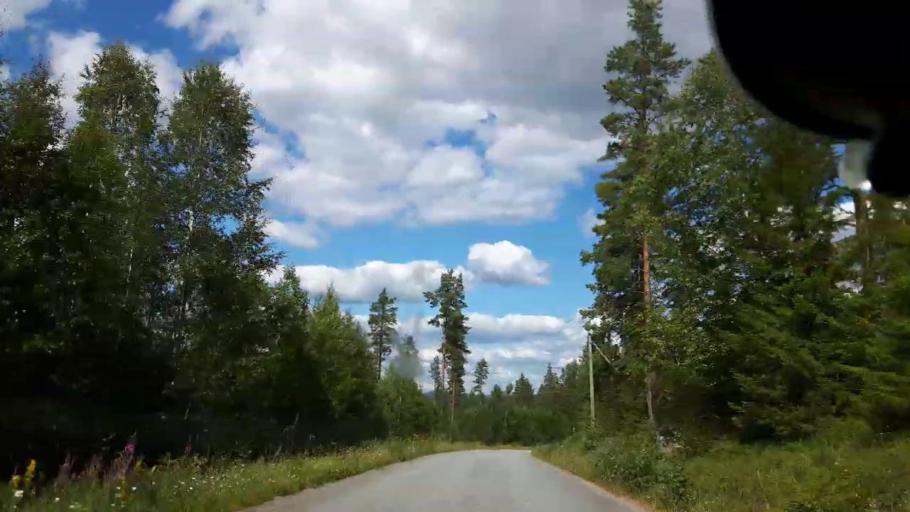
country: SE
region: Jaemtland
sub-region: Ragunda Kommun
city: Hammarstrand
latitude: 62.9323
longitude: 16.6934
